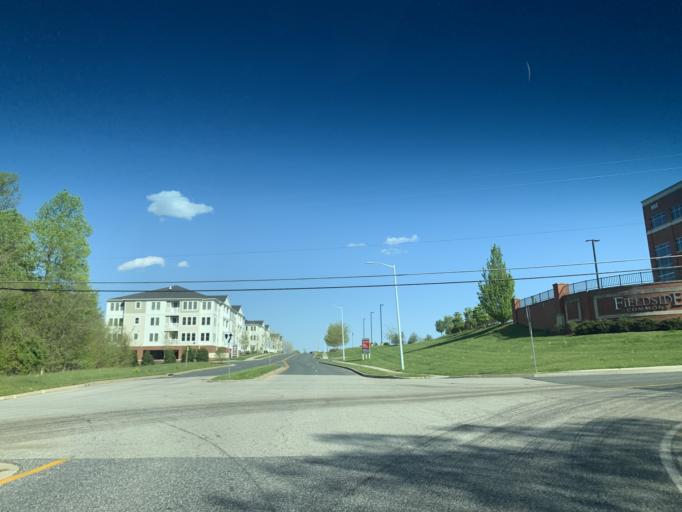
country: US
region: Maryland
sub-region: Harford County
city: Aberdeen
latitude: 39.5334
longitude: -76.1925
